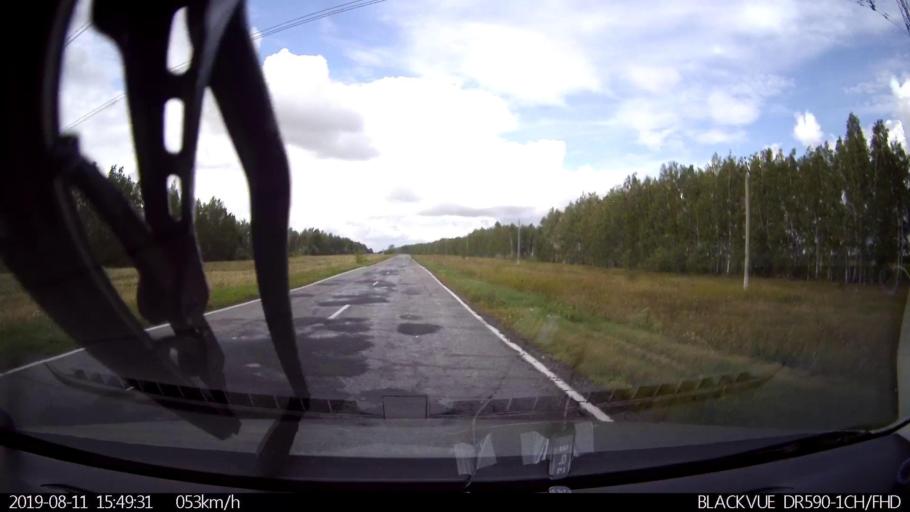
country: RU
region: Ulyanovsk
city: Ignatovka
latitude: 53.9049
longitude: 47.6551
